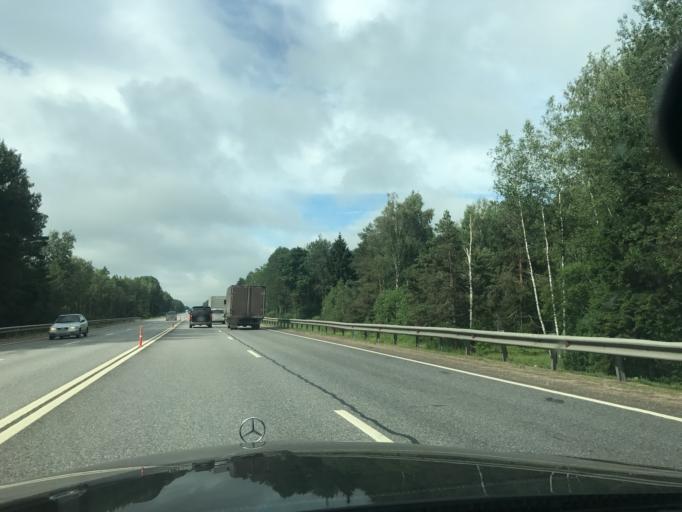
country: RU
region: Smolensk
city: Kardymovo
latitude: 55.0067
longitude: 32.2839
